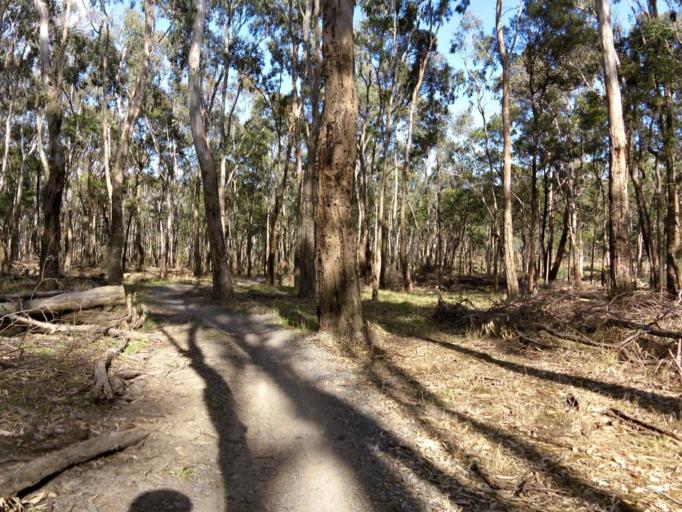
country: AU
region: Victoria
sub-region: Yarra Ranges
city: Lysterfield
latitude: -37.9354
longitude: 145.2958
